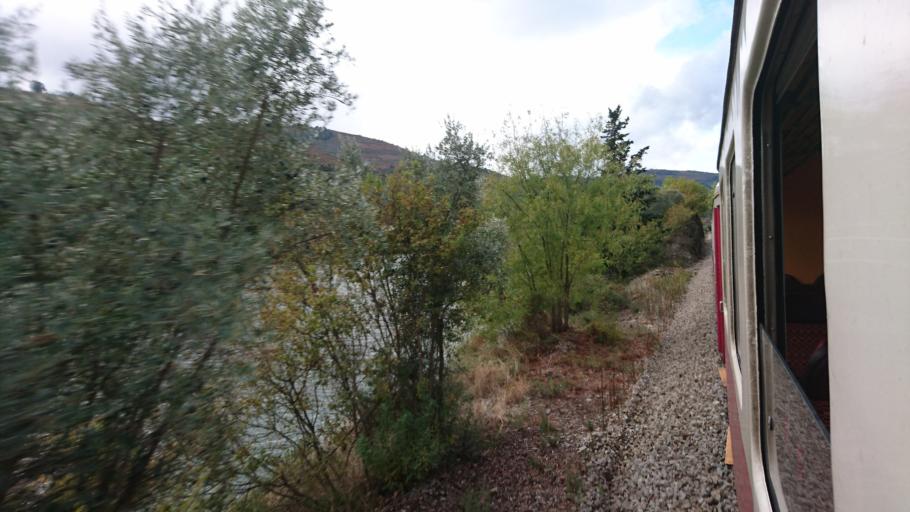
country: PT
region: Viseu
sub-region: Tabuaco
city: Tabuaco
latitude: 41.1715
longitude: -7.5620
